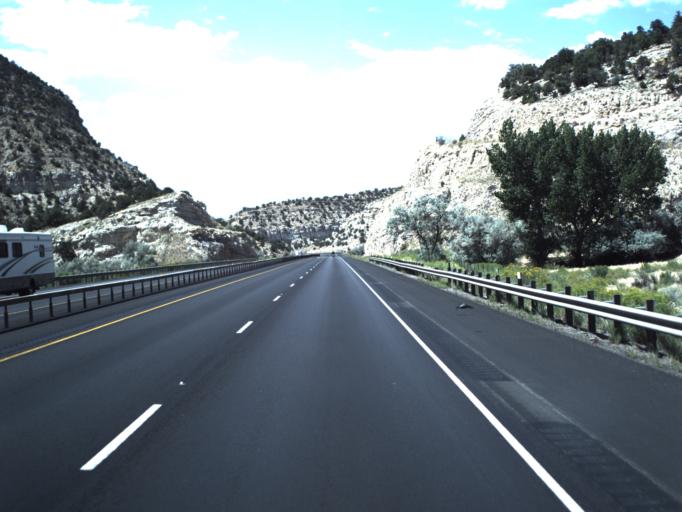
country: US
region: Utah
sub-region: Sevier County
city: Salina
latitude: 38.9075
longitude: -111.6960
